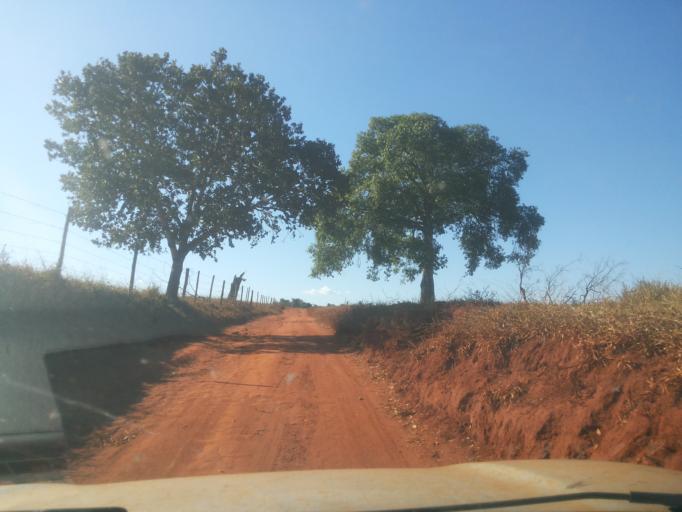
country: BR
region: Minas Gerais
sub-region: Centralina
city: Centralina
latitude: -18.7512
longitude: -49.1881
